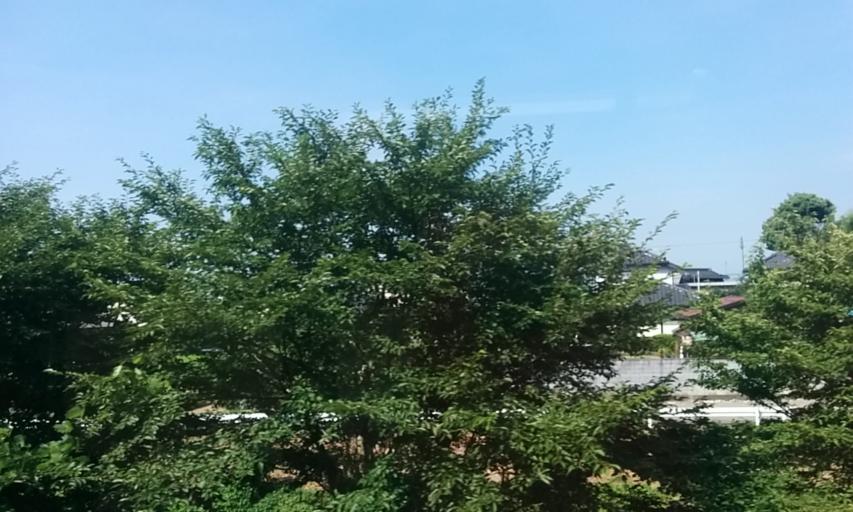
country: JP
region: Saitama
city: Kukichuo
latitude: 36.0995
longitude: 139.6539
